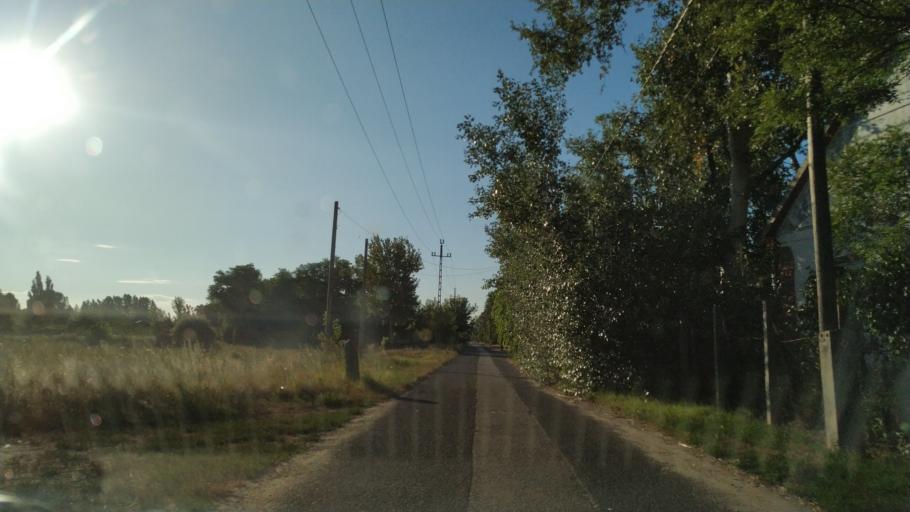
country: HU
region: Pest
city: Nagykata
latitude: 47.4014
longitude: 19.7438
